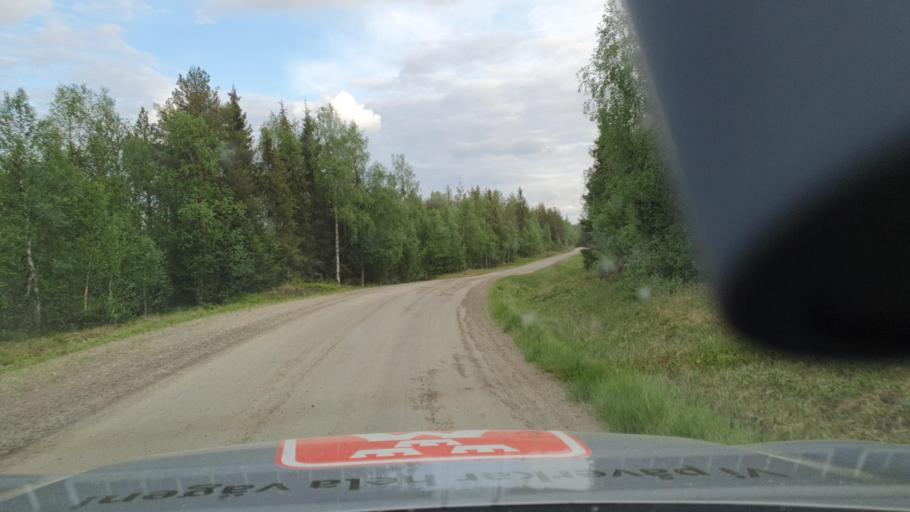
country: SE
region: Norrbotten
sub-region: Gallivare Kommun
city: Gaellivare
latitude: 66.7371
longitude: 21.1408
